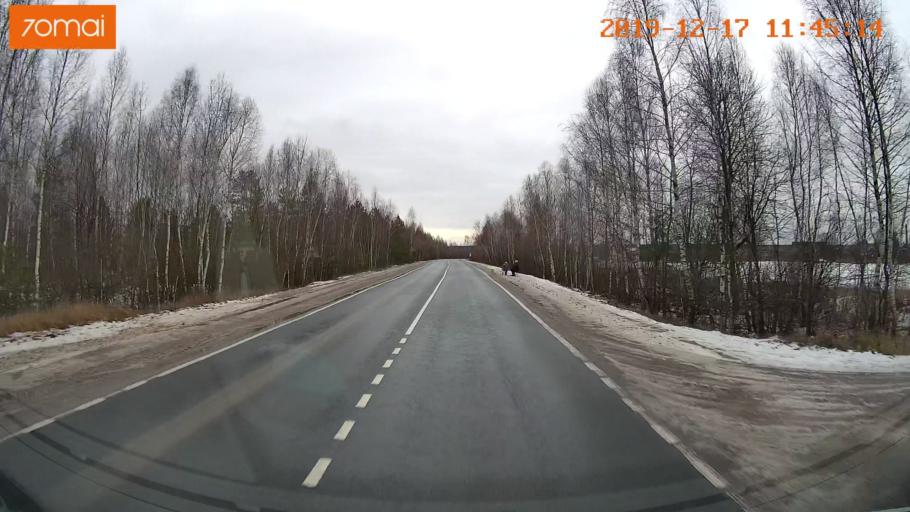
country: RU
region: Vladimir
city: Velikodvorskiy
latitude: 55.2528
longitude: 40.6713
